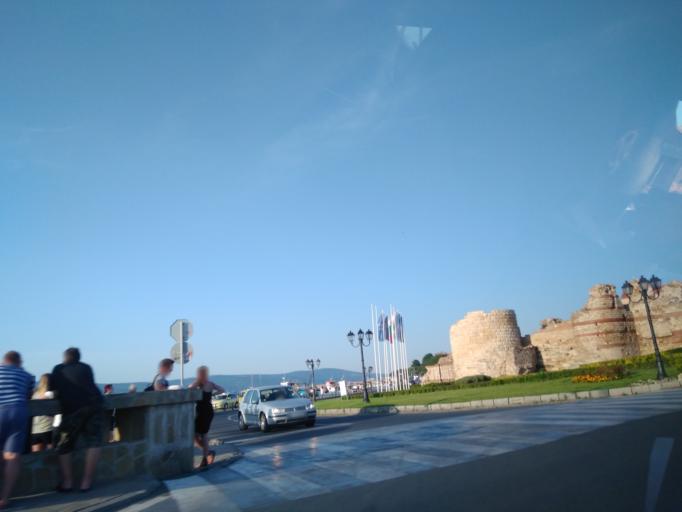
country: BG
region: Burgas
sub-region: Obshtina Nesebur
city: Nesebar
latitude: 42.6590
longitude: 27.7299
